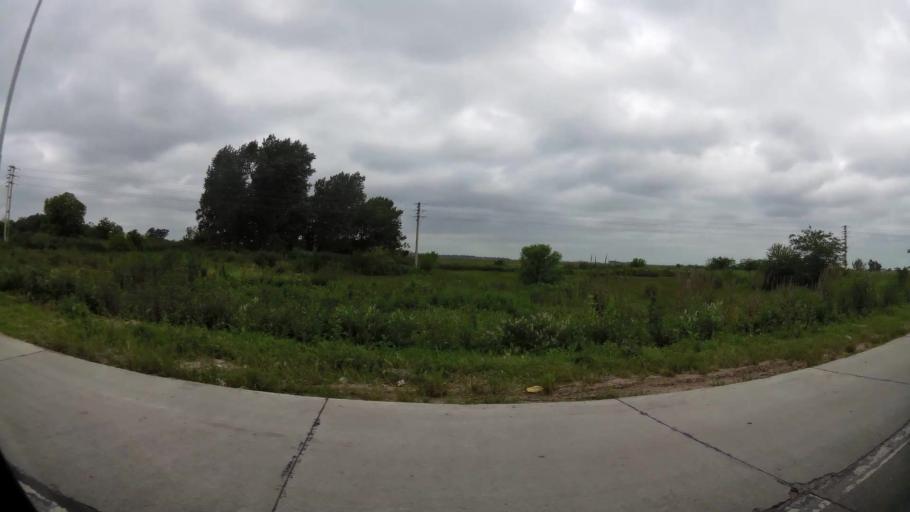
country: AR
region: Buenos Aires
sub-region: Partido de San Vicente
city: San Vicente
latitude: -35.0550
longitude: -58.4411
